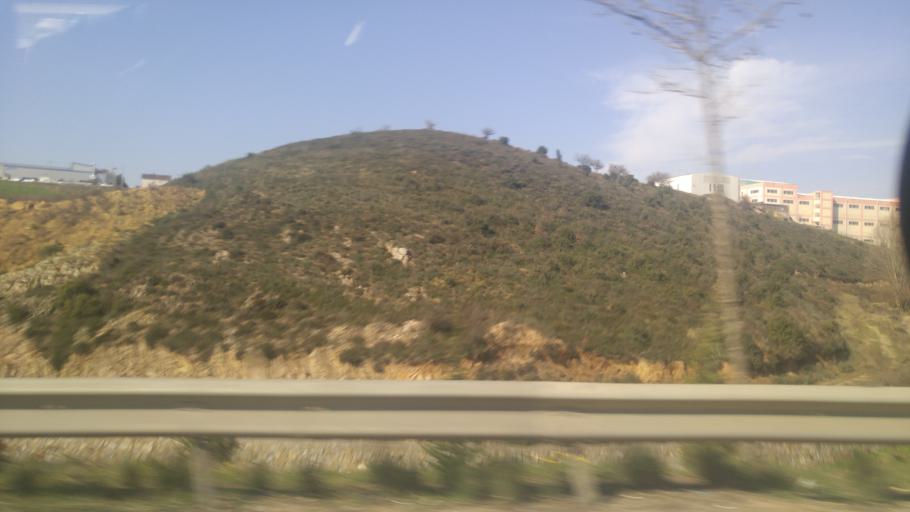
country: TR
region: Kocaeli
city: Balcik
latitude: 40.8459
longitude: 29.3747
